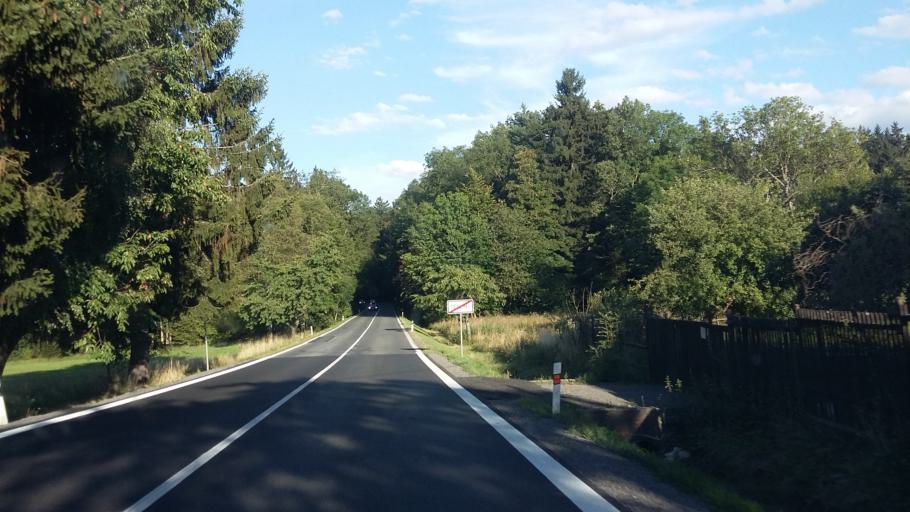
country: CZ
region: Central Bohemia
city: Rozmital pod Tremsinem
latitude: 49.6225
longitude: 13.7583
